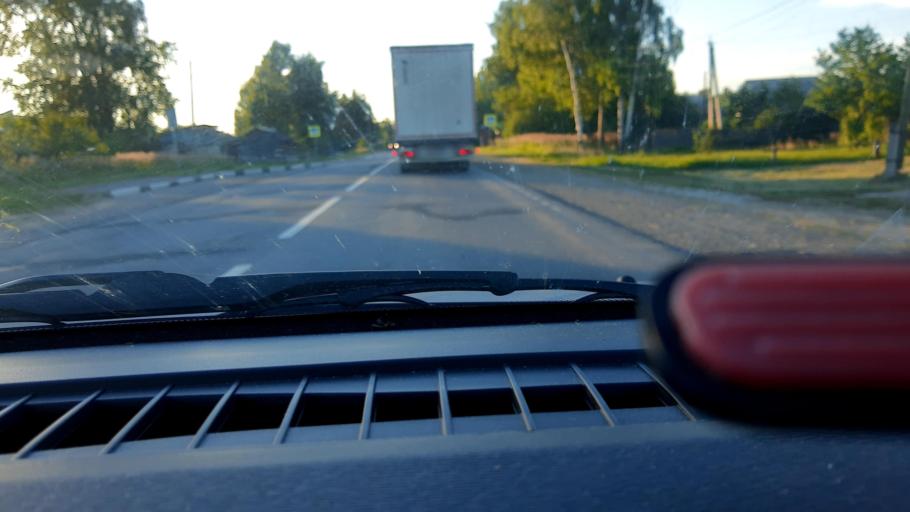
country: RU
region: Nizjnij Novgorod
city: Uren'
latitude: 57.3431
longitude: 45.7098
